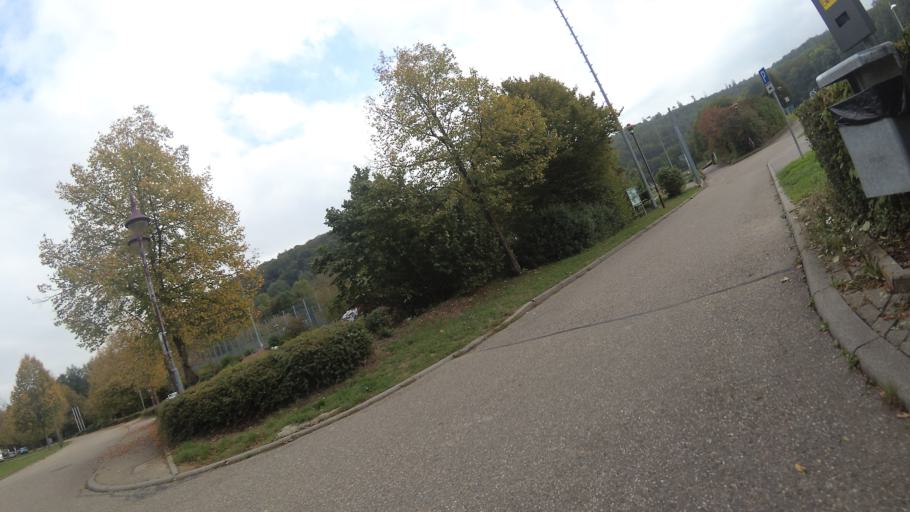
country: DE
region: Baden-Wuerttemberg
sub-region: Regierungsbezirk Stuttgart
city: Eberstadt
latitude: 49.2072
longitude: 9.2938
